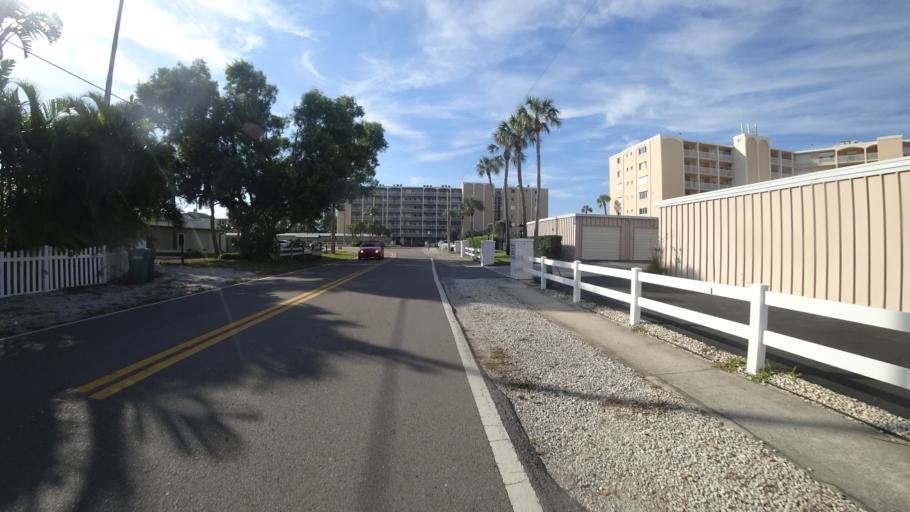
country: US
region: Florida
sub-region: Manatee County
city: Holmes Beach
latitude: 27.5067
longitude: -82.7172
